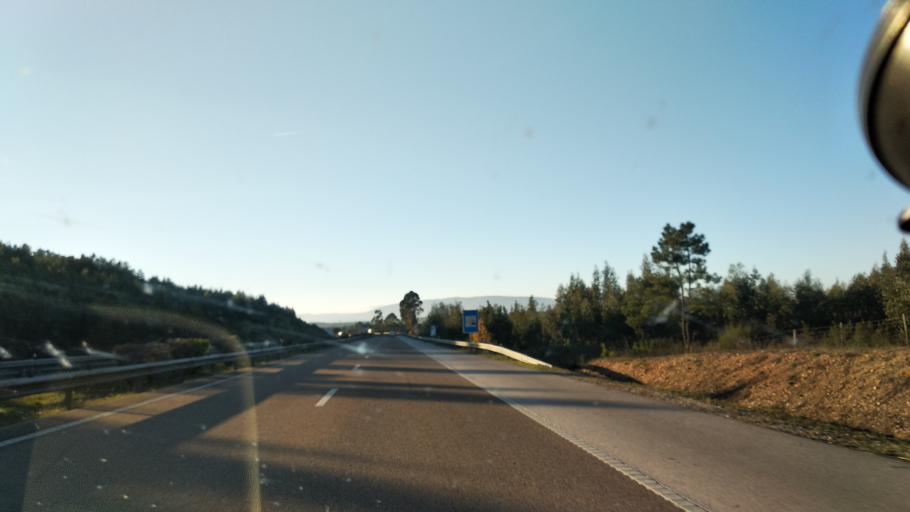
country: PT
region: Santarem
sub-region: Chamusca
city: Vila Nova da Barquinha
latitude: 39.4902
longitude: -8.4334
